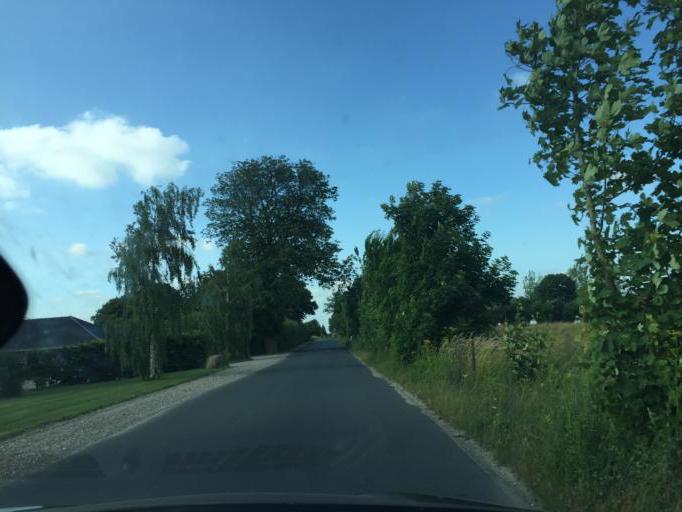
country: DK
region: South Denmark
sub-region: Kerteminde Kommune
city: Langeskov
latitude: 55.3260
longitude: 10.5426
